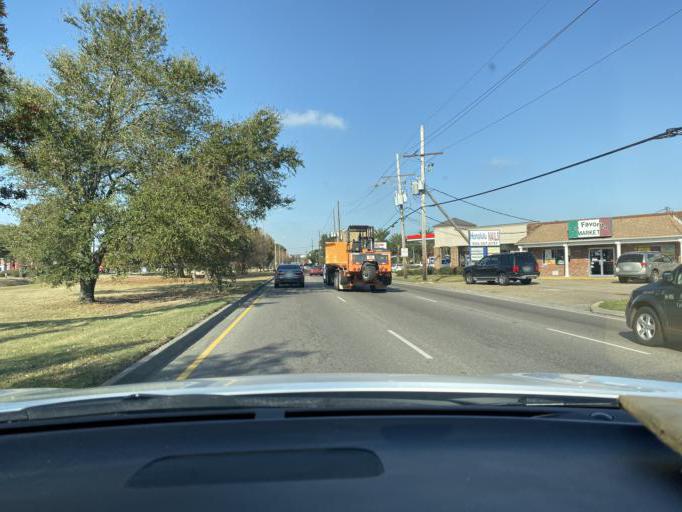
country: US
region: Louisiana
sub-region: Jefferson Parish
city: Terrytown
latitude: 29.9234
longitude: -90.0179
